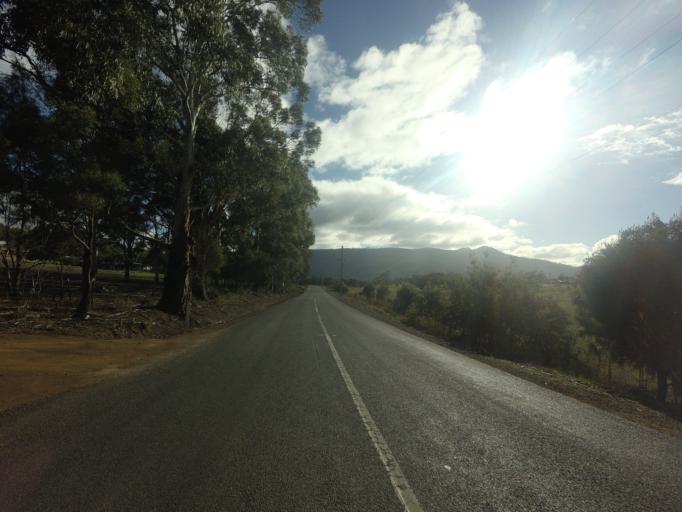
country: AU
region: Tasmania
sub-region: Derwent Valley
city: New Norfolk
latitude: -42.7887
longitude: 147.1209
